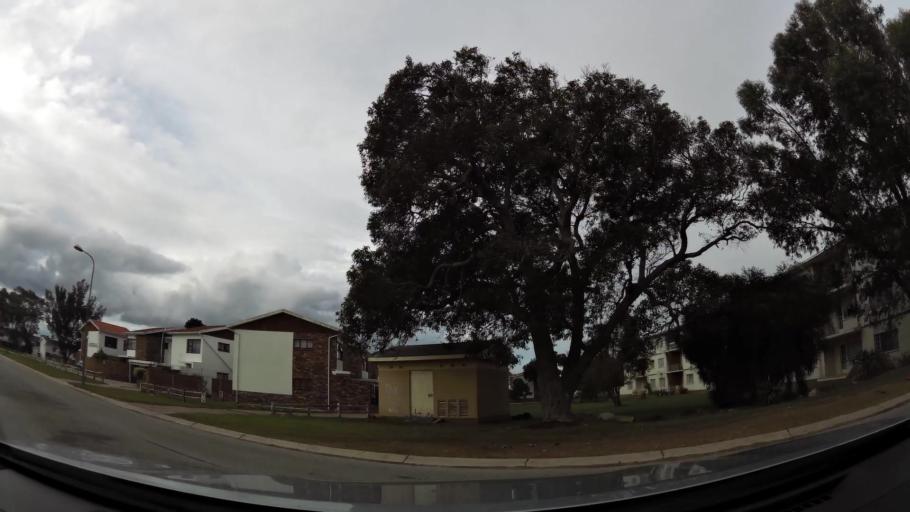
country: ZA
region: Eastern Cape
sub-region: Nelson Mandela Bay Metropolitan Municipality
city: Port Elizabeth
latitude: -33.9408
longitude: 25.4953
